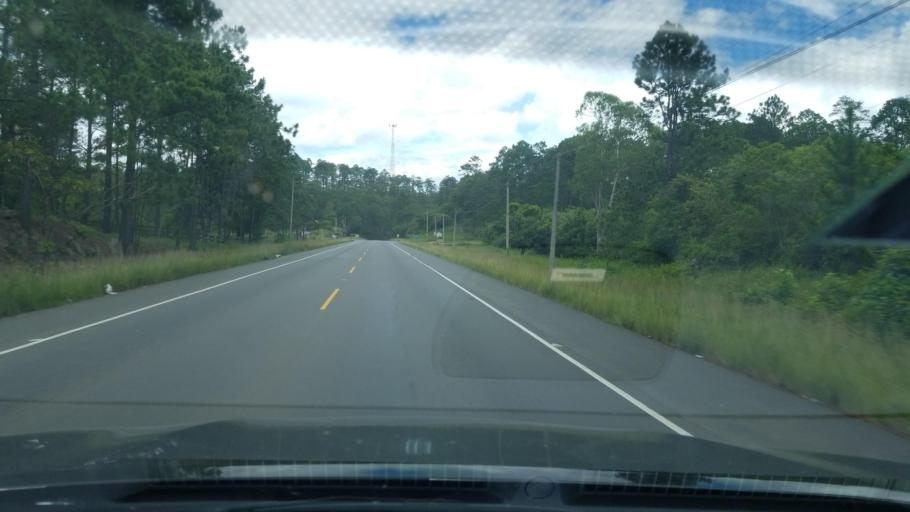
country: HN
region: Francisco Morazan
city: Talanga
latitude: 14.3548
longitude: -87.1539
